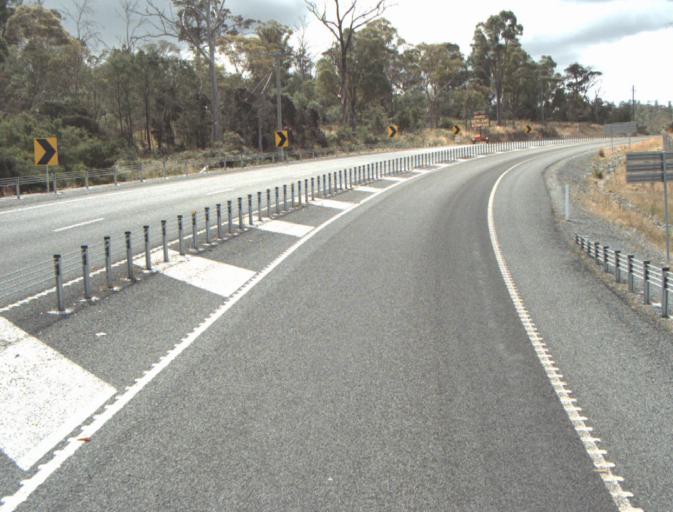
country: AU
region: Tasmania
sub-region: Launceston
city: Mayfield
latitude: -41.2998
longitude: 147.0495
